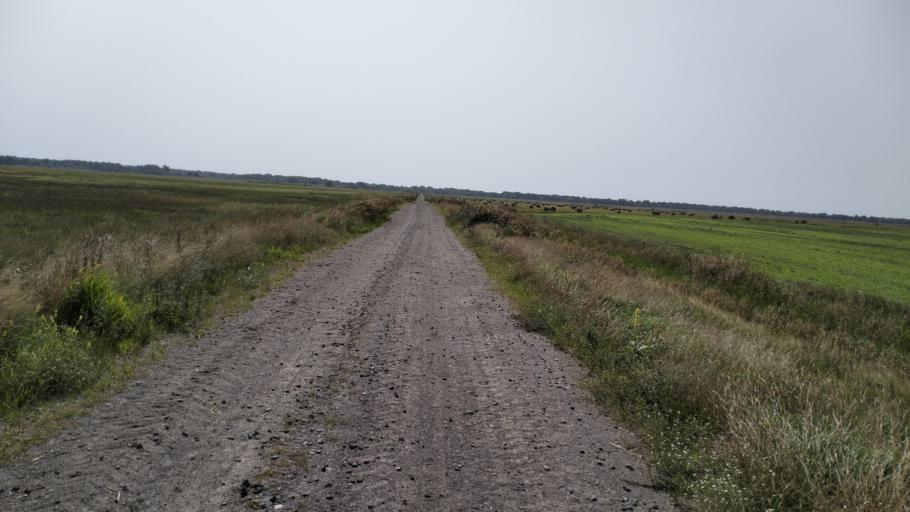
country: BY
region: Brest
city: Davyd-Haradok
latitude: 51.9832
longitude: 27.1751
